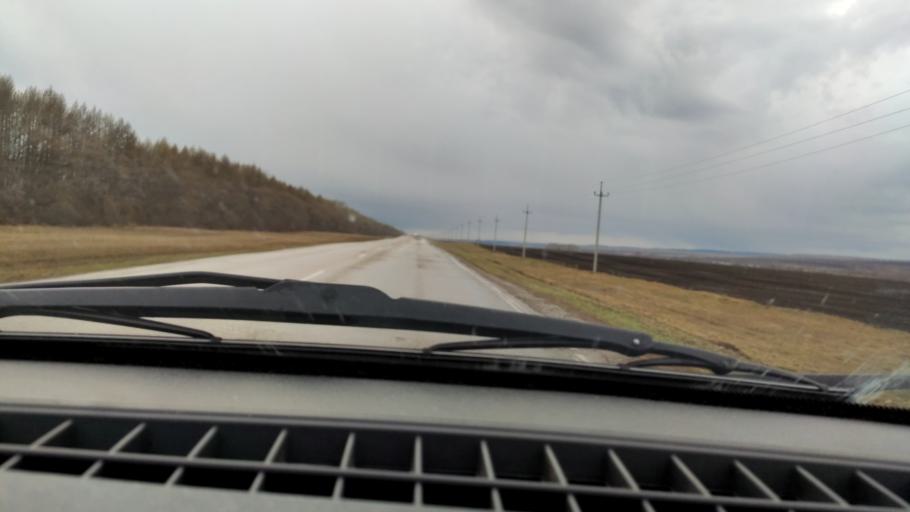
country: RU
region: Bashkortostan
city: Chekmagush
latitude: 55.1102
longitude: 54.9340
